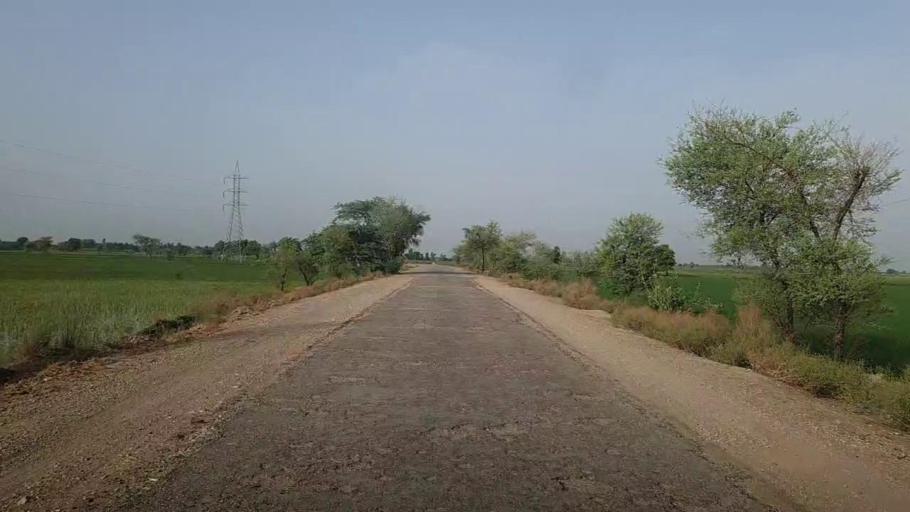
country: PK
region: Sindh
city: Mehar
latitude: 27.1391
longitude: 67.7914
